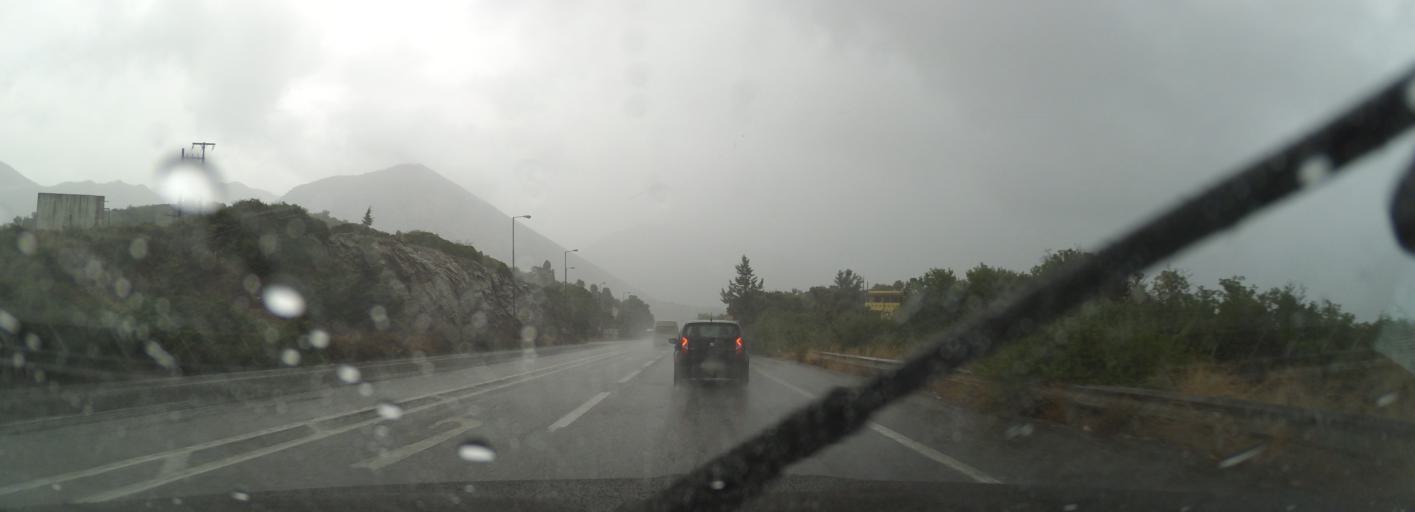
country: GR
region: Crete
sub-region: Nomos Rethymnis
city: Anogeia
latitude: 35.3935
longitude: 24.8898
